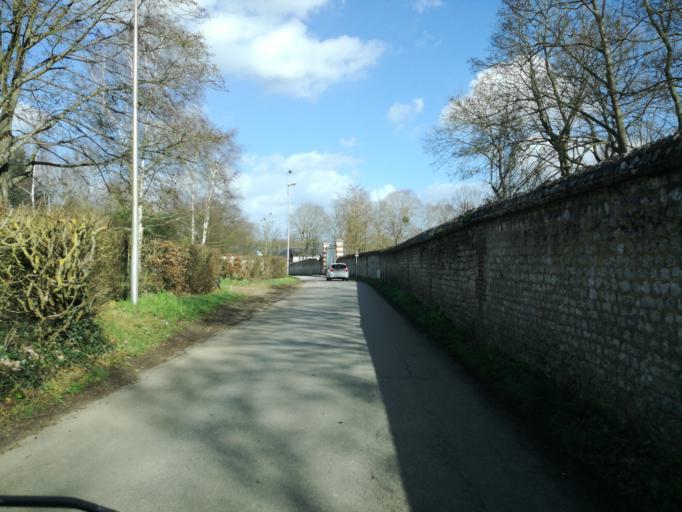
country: FR
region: Haute-Normandie
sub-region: Departement de la Seine-Maritime
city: Grand-Couronne
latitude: 49.3598
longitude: 0.9747
